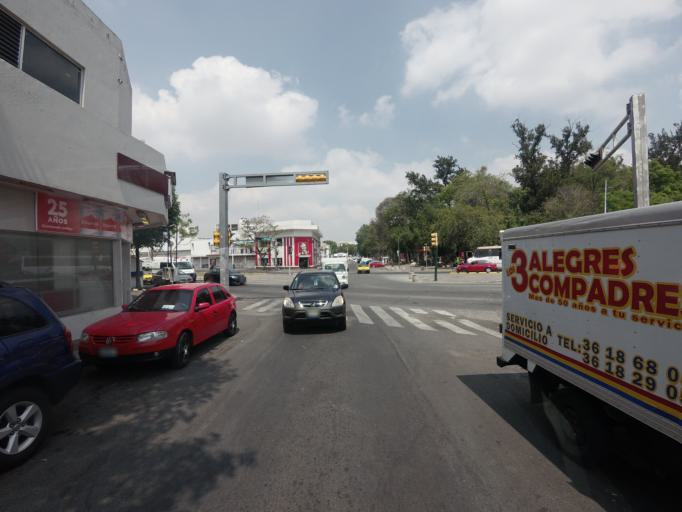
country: MX
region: Jalisco
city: Guadalajara
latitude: 20.6793
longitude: -103.3394
